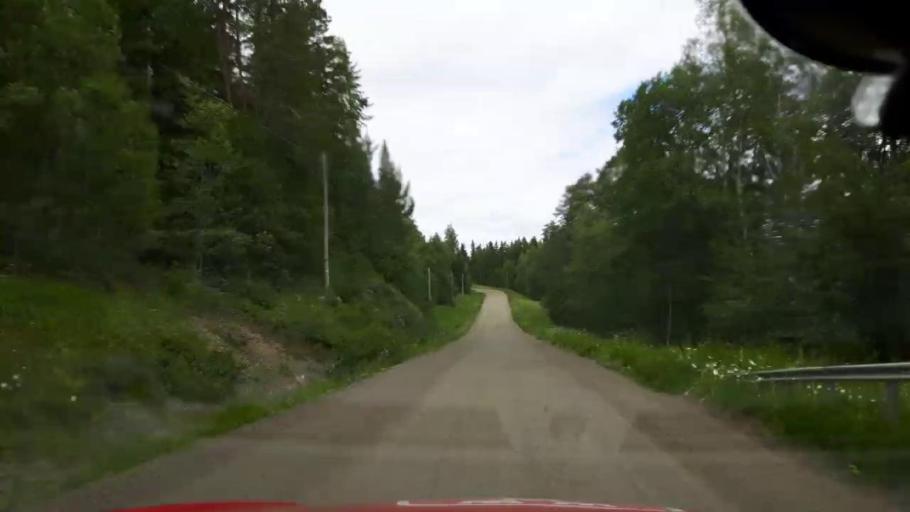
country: SE
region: Jaemtland
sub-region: OEstersunds Kommun
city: Brunflo
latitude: 62.9036
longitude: 15.1098
